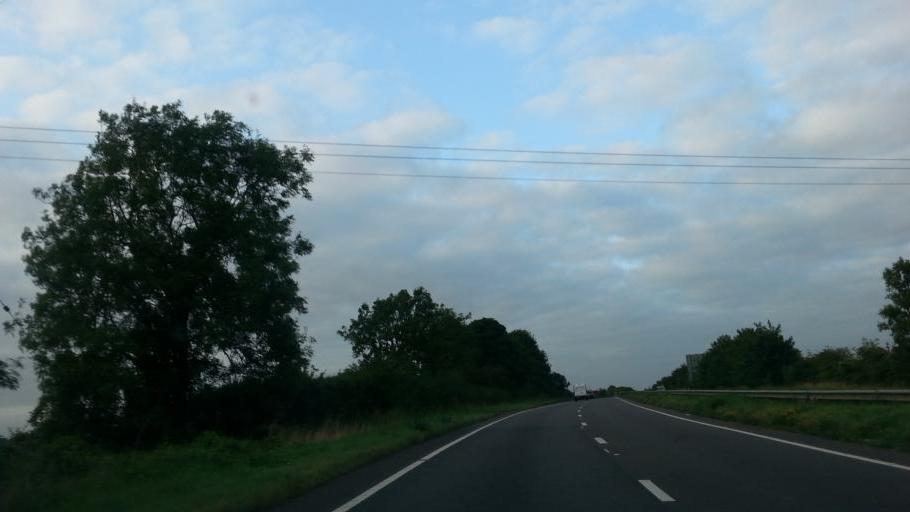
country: GB
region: England
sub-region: Northamptonshire
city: Brackley
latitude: 51.9990
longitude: -1.1607
